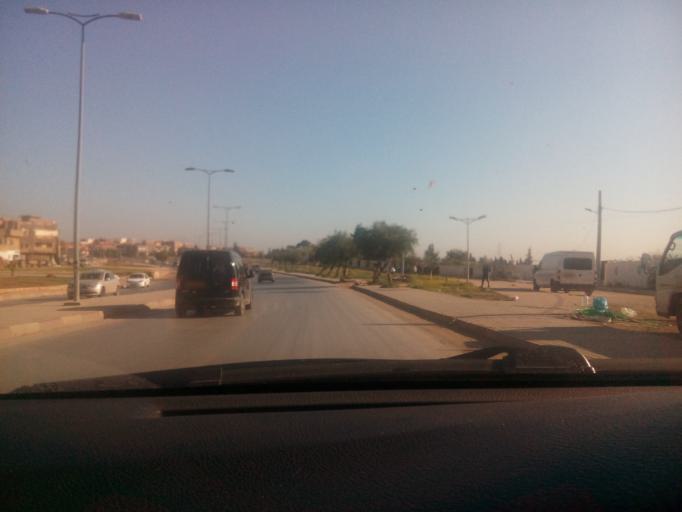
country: DZ
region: Oran
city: Oran
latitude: 35.6615
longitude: -0.6873
